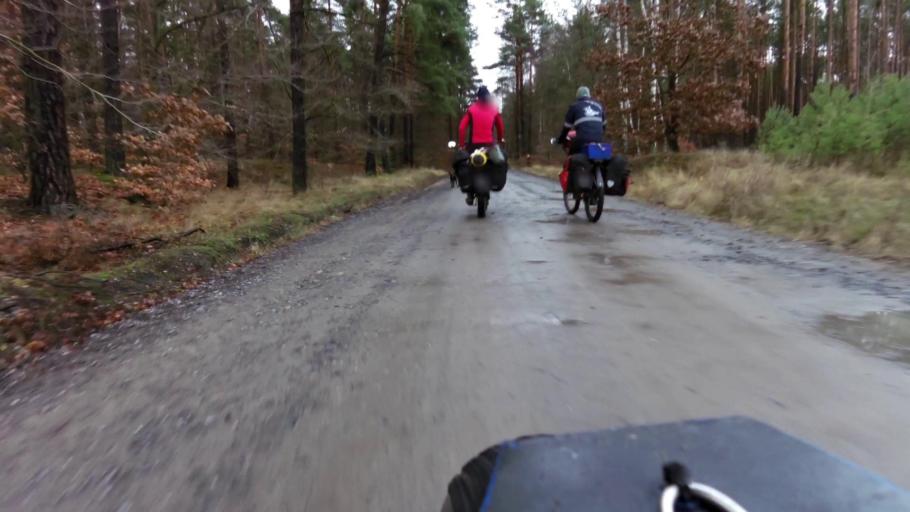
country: PL
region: Lubusz
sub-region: Powiat gorzowski
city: Witnica
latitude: 52.6984
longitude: 14.8415
